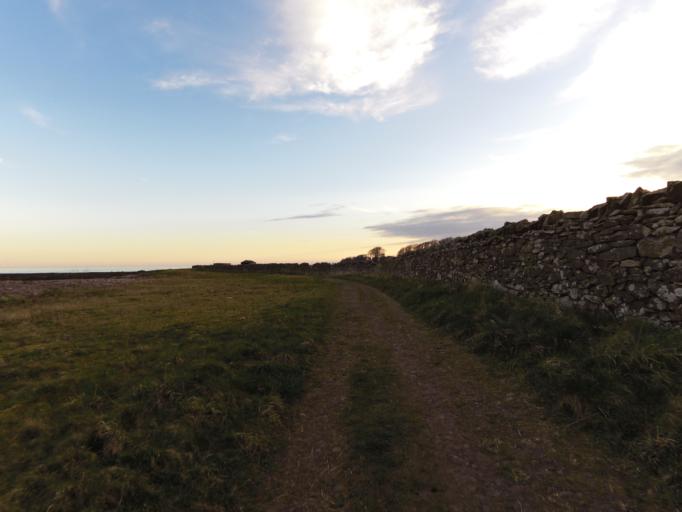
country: GB
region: Scotland
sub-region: Aberdeenshire
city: Inverbervie
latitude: 56.8042
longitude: -2.3146
